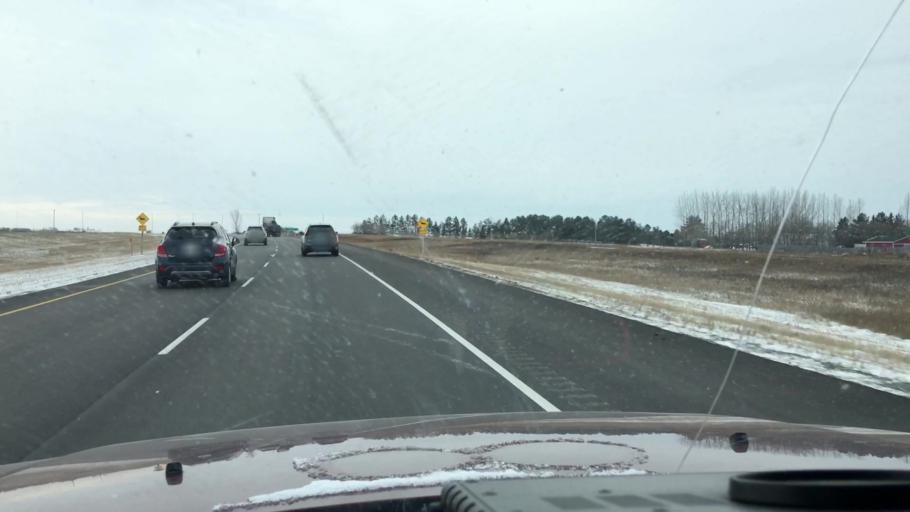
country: CA
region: Saskatchewan
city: Saskatoon
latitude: 51.8569
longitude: -106.5082
